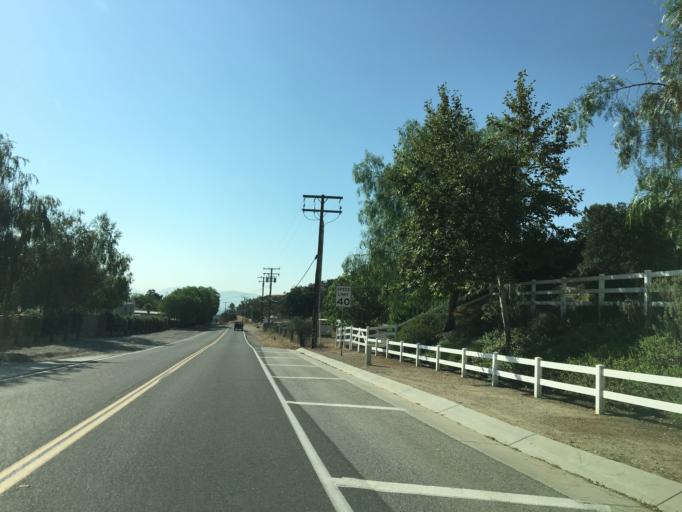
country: US
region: California
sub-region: Los Angeles County
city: Val Verde
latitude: 34.4663
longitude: -118.6650
